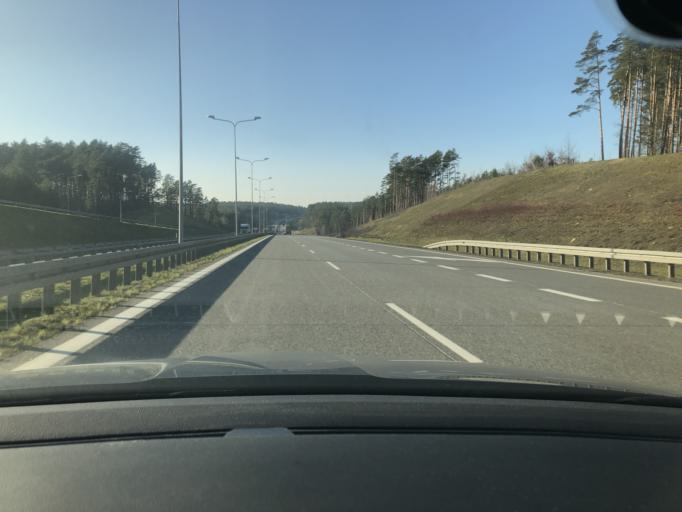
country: PL
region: Lubusz
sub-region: Powiat sulecinski
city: Torzym
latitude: 52.3250
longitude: 15.0829
